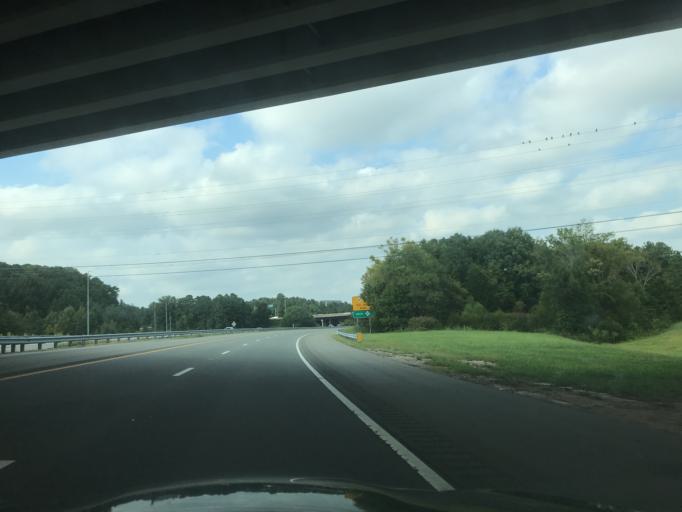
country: US
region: North Carolina
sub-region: Wake County
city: Morrisville
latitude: 35.8975
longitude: -78.8761
